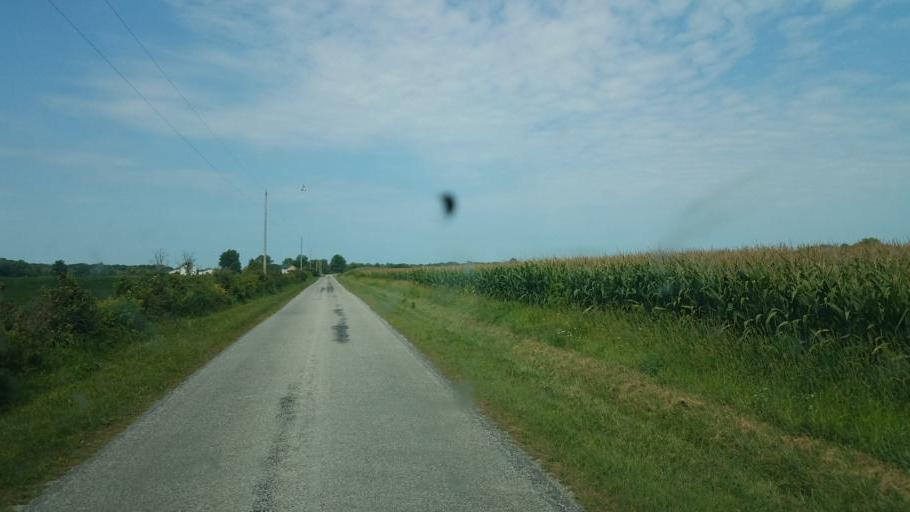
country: US
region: Ohio
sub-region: Delaware County
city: Ashley
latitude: 40.4427
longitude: -83.0263
